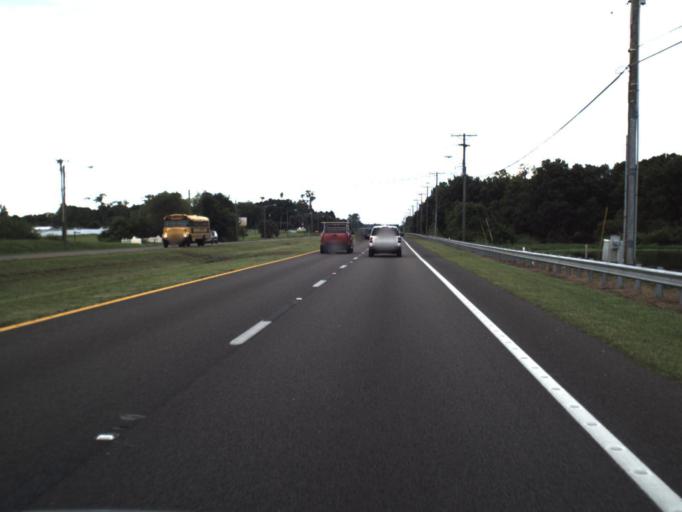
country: US
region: Florida
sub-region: Polk County
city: Mulberry
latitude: 27.9160
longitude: -81.9738
